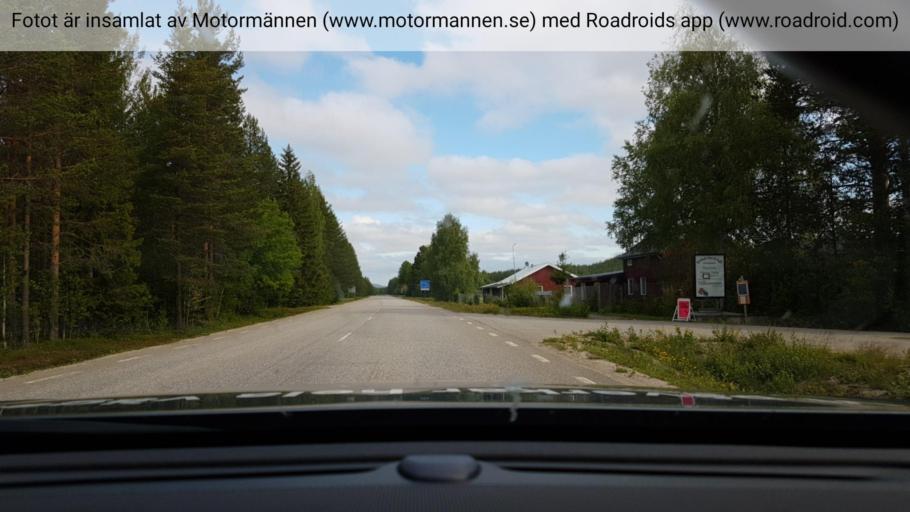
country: SE
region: Vaesterbotten
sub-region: Norsjo Kommun
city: Norsjoe
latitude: 64.5775
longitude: 19.3050
